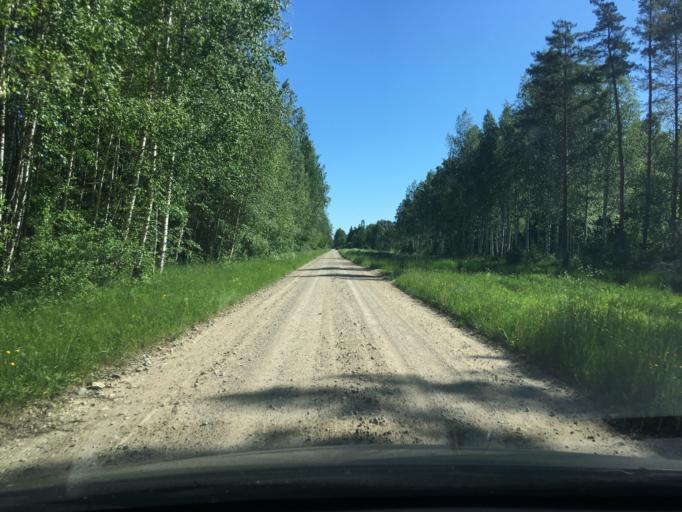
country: EE
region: Laeaene
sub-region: Lihula vald
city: Lihula
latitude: 58.6436
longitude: 23.7743
